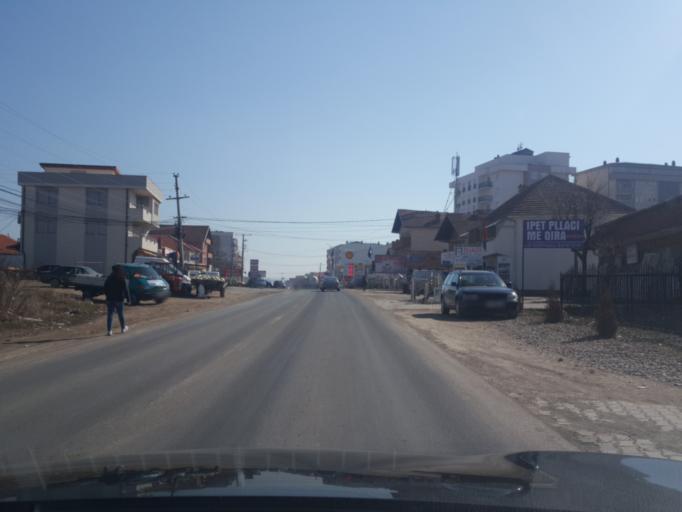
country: XK
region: Mitrovica
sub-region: Vushtrri
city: Vushtrri
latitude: 42.8289
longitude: 20.9670
